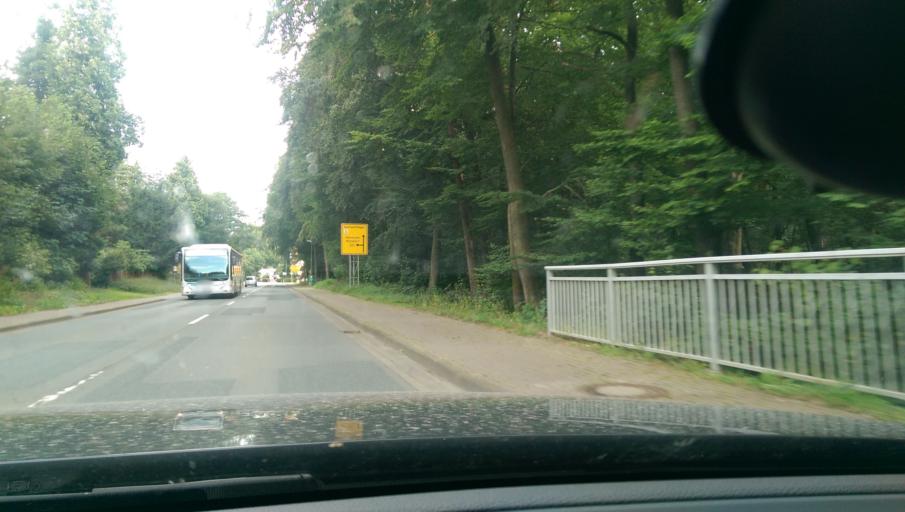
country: DE
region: Lower Saxony
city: Rehburg-Loccum
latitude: 52.4376
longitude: 9.2054
